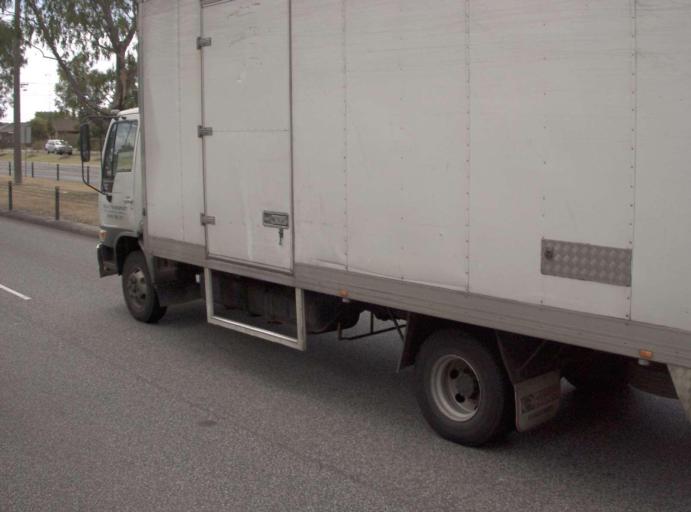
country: AU
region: Victoria
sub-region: Greater Dandenong
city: Keysborough
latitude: -37.9940
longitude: 145.1705
